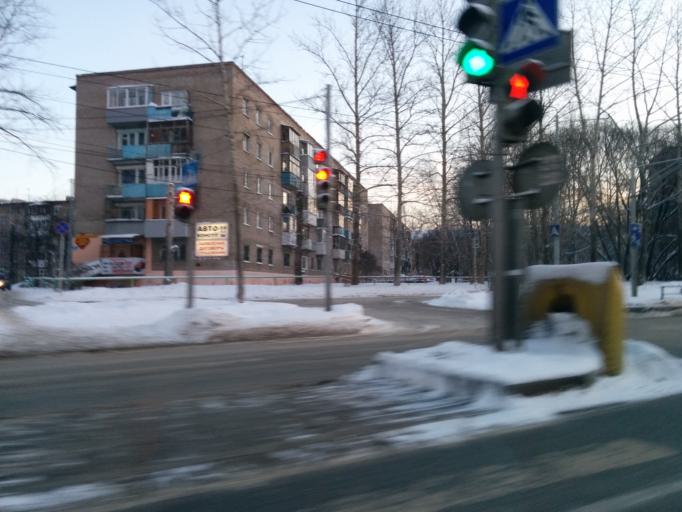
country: RU
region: Perm
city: Perm
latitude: 57.9930
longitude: 56.2909
